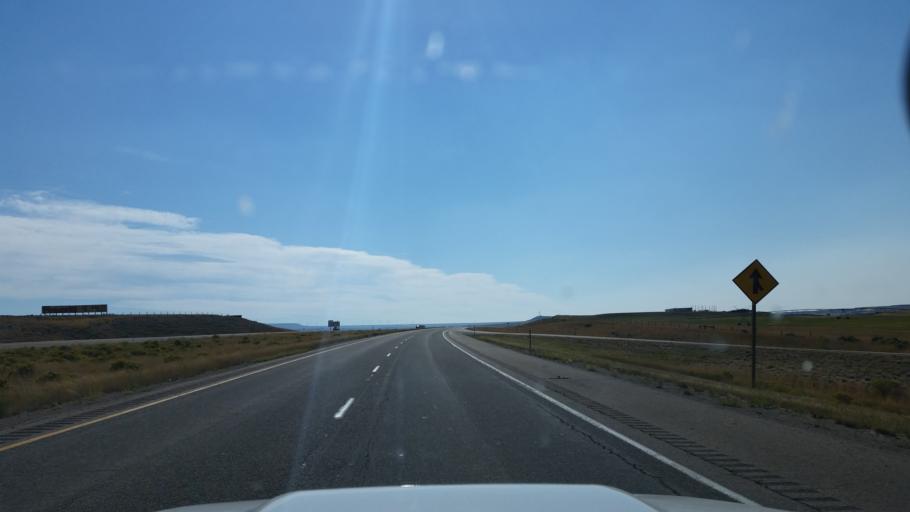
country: US
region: Wyoming
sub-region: Uinta County
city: Lyman
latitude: 41.3562
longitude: -110.3409
